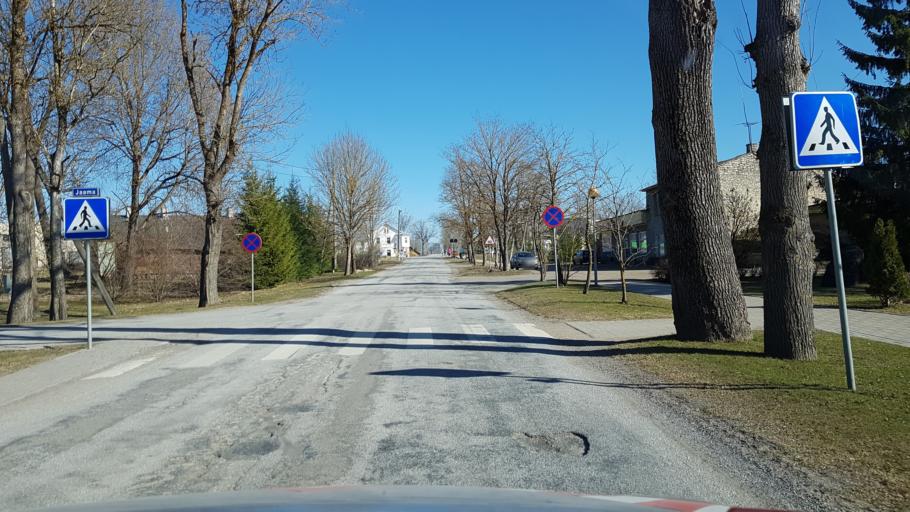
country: EE
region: Laeaene-Virumaa
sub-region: Rakke vald
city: Rakke
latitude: 58.9884
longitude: 26.2409
